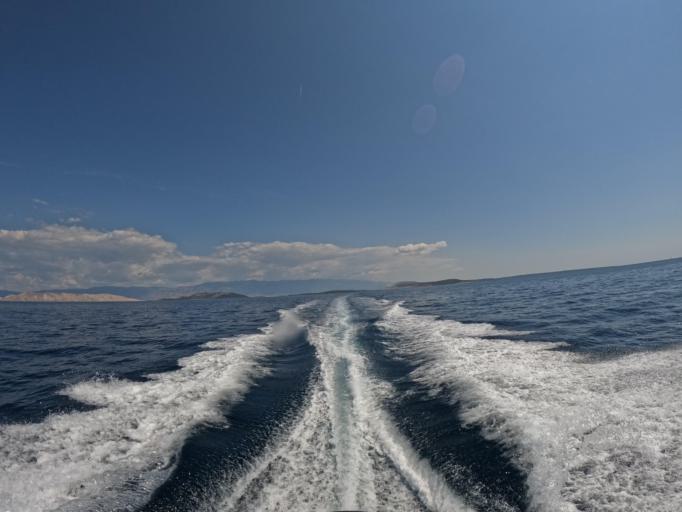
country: HR
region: Primorsko-Goranska
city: Lopar
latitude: 44.8832
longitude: 14.6465
